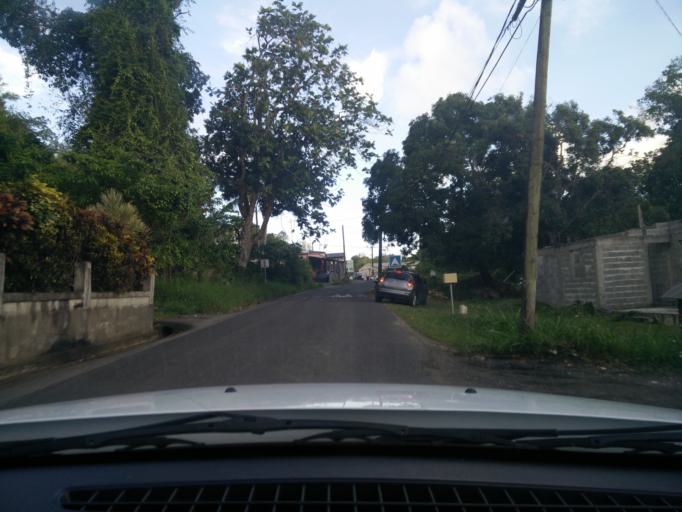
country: GP
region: Guadeloupe
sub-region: Guadeloupe
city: Les Abymes
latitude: 16.2524
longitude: -61.4991
